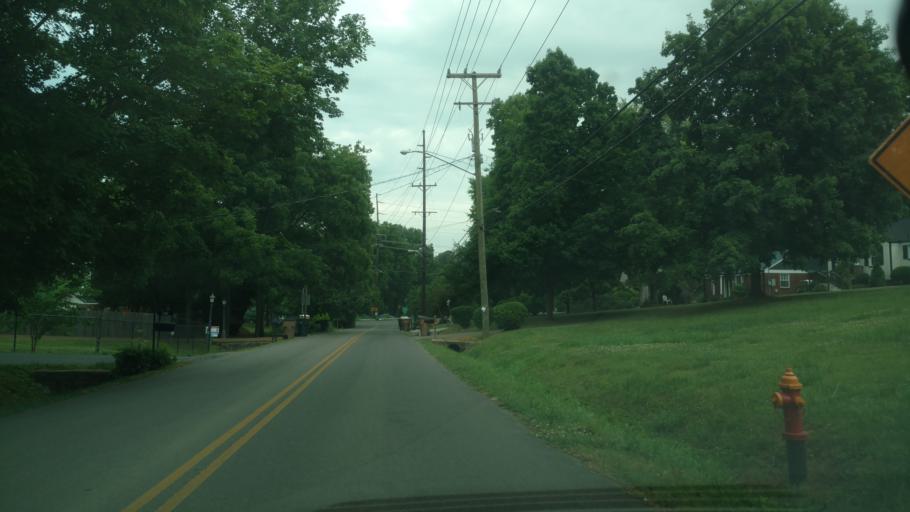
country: US
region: Tennessee
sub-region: Davidson County
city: Nashville
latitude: 36.1956
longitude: -86.7103
